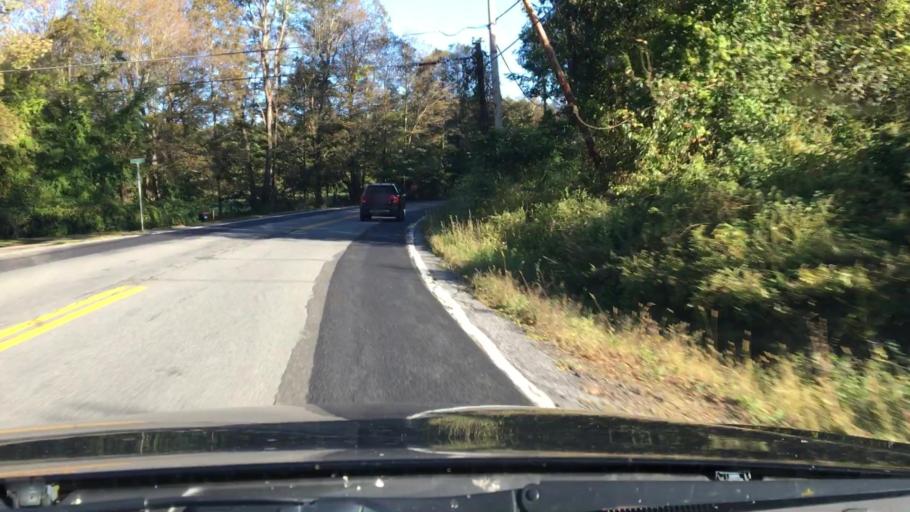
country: US
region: Connecticut
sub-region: Fairfield County
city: Sherman
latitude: 41.6530
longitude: -73.5318
